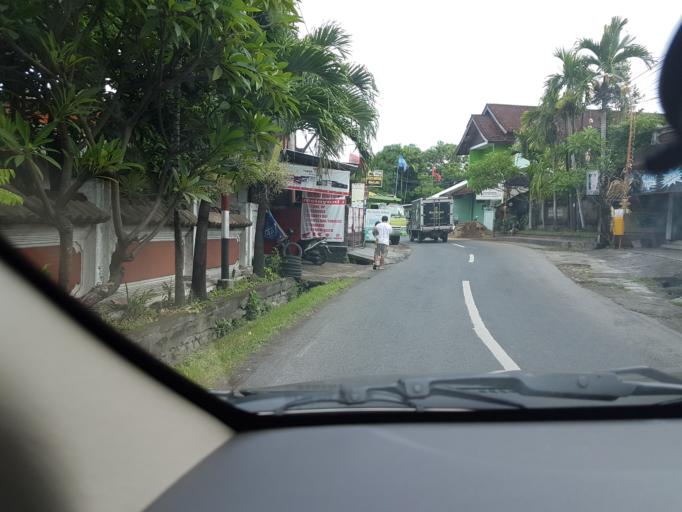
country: ID
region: Bali
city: Denpasar
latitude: -8.6680
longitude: 115.1916
